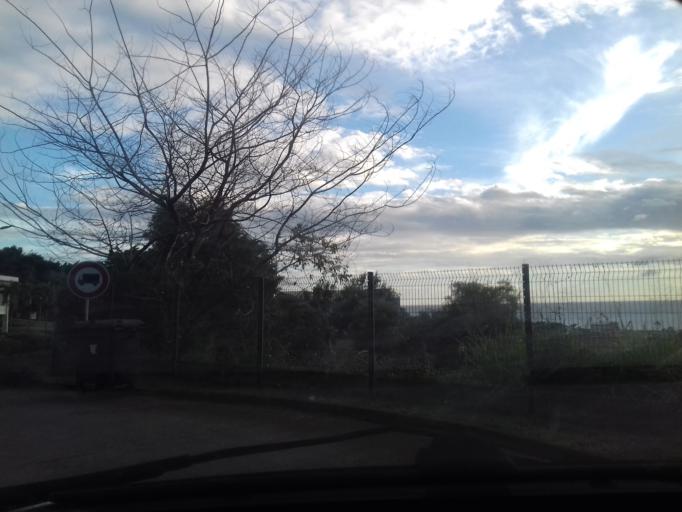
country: MQ
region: Martinique
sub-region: Martinique
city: Fort-de-France
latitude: 14.6205
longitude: -61.0953
